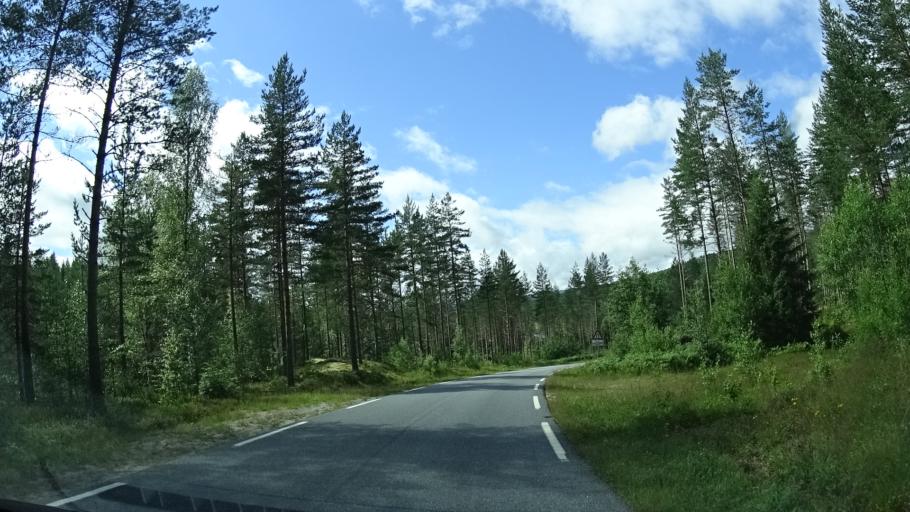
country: NO
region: Buskerud
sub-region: Krodsherad
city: Noresund
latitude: 60.2273
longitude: 9.8365
